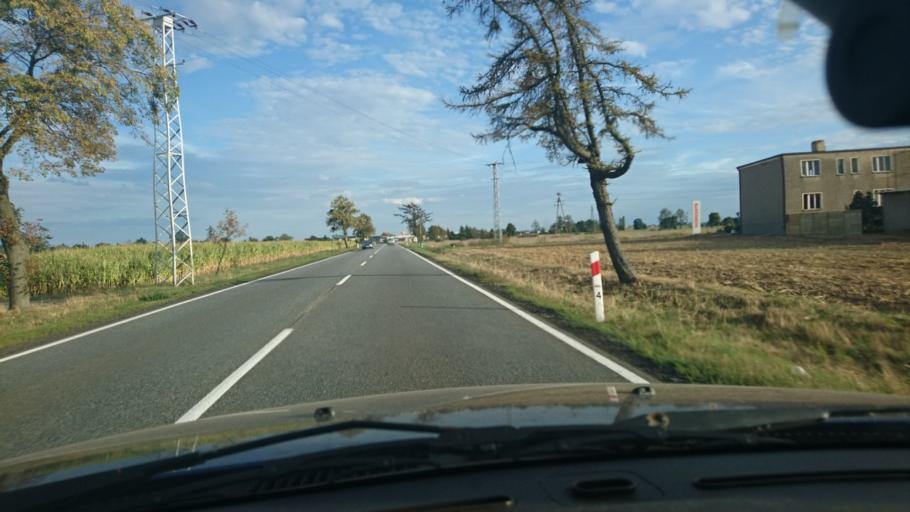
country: PL
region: Opole Voivodeship
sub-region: Powiat kluczborski
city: Kluczbork
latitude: 51.0125
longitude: 18.2024
